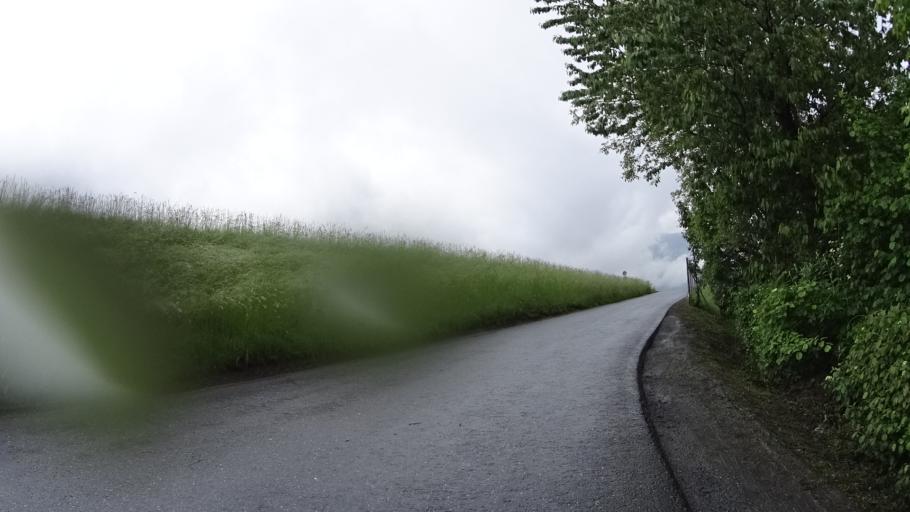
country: LI
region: Balzers
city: Balzers
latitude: 47.0732
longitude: 9.4929
